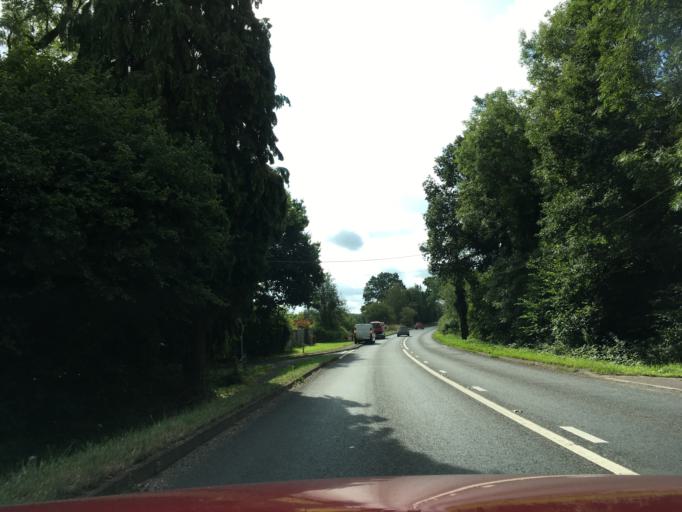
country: GB
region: England
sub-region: Hampshire
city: Bishops Waltham
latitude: 50.9664
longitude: -1.2422
